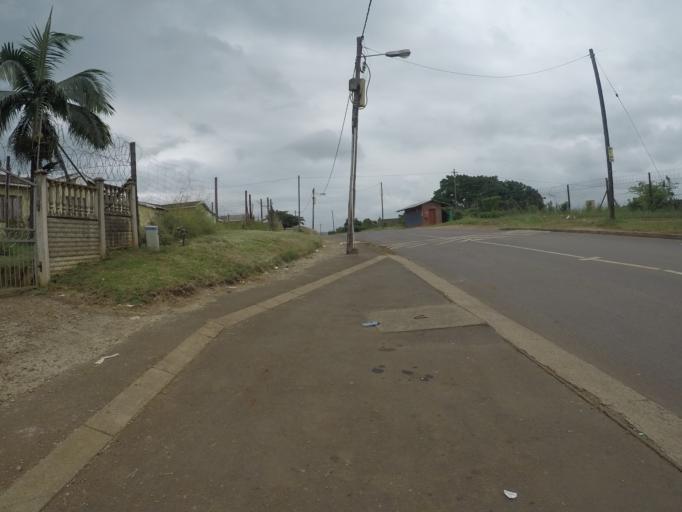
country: ZA
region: KwaZulu-Natal
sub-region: uThungulu District Municipality
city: Empangeni
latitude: -28.7830
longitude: 31.8562
